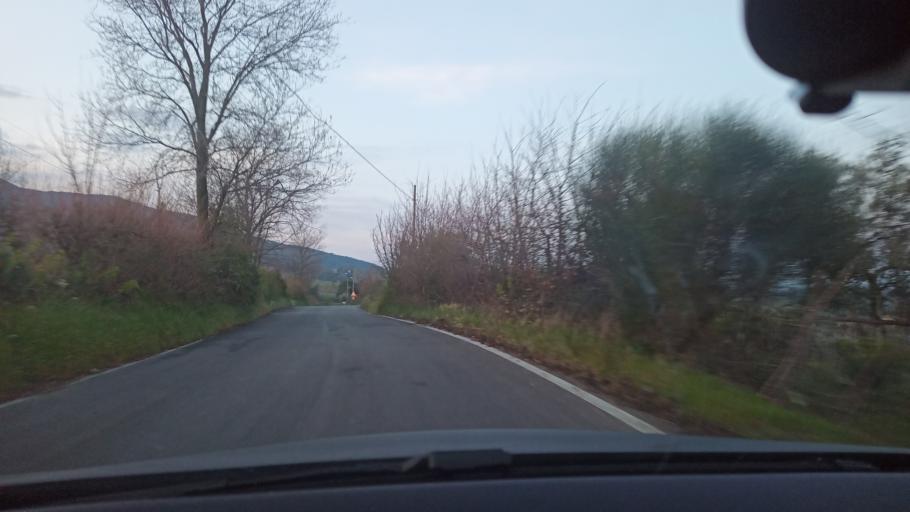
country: IT
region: Latium
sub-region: Provincia di Rieti
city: Montasola
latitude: 42.3682
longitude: 12.6761
